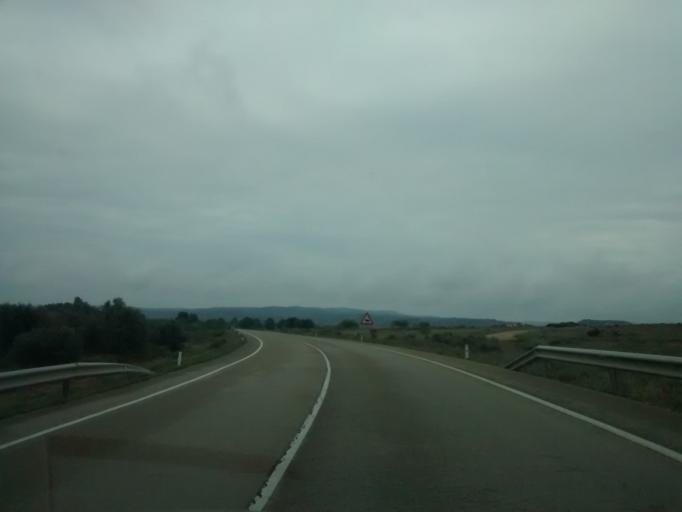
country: ES
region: Aragon
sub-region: Provincia de Zaragoza
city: Caspe
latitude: 41.2142
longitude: -0.0063
